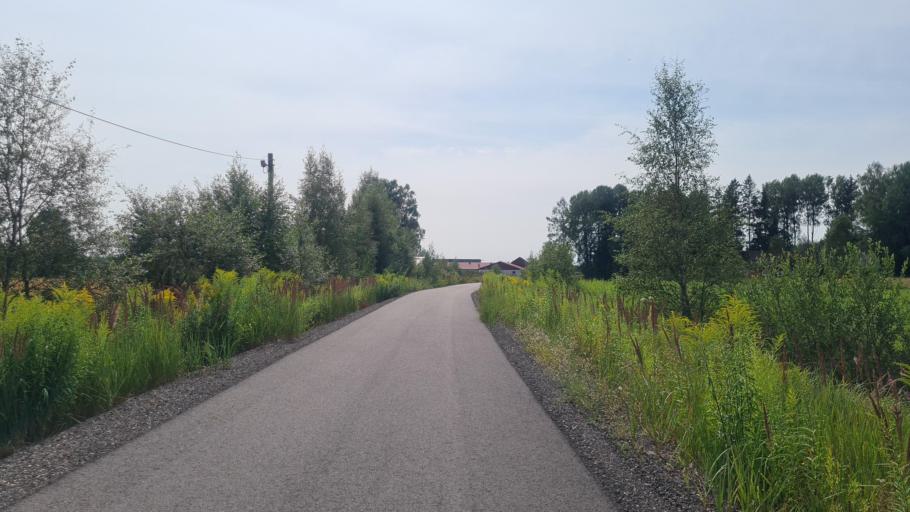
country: SE
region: Kronoberg
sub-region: Ljungby Kommun
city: Lagan
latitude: 56.9060
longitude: 13.9908
